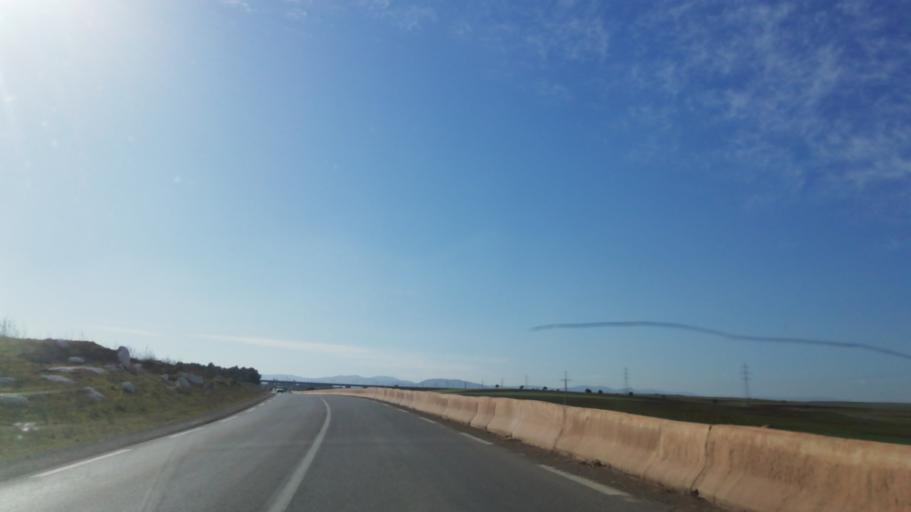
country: DZ
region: Tlemcen
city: Ouled Mimoun
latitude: 35.0167
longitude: -0.9046
